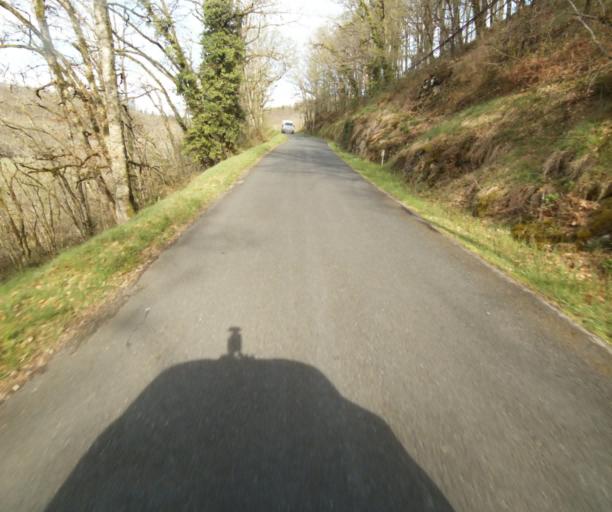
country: FR
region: Limousin
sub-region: Departement de la Correze
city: Naves
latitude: 45.3432
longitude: 1.8208
